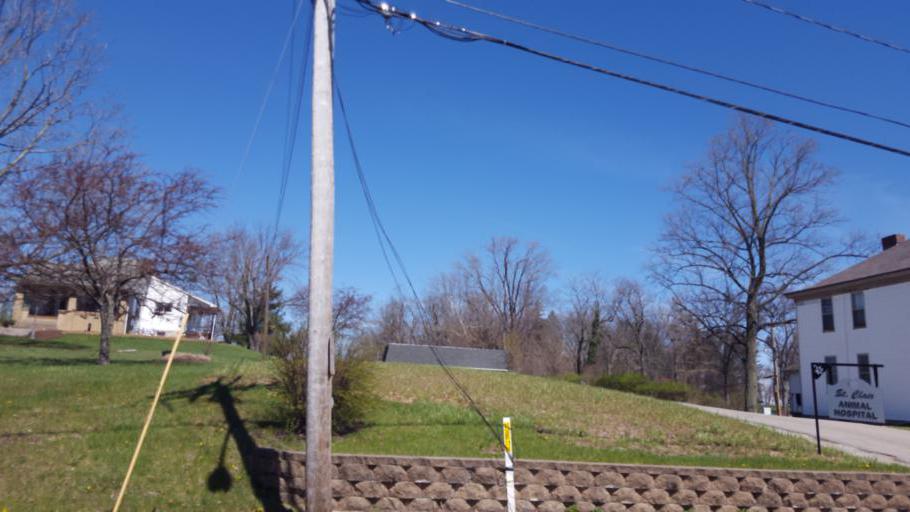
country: US
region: Ohio
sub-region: Belmont County
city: Saint Clairsville
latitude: 40.0834
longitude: -80.8890
